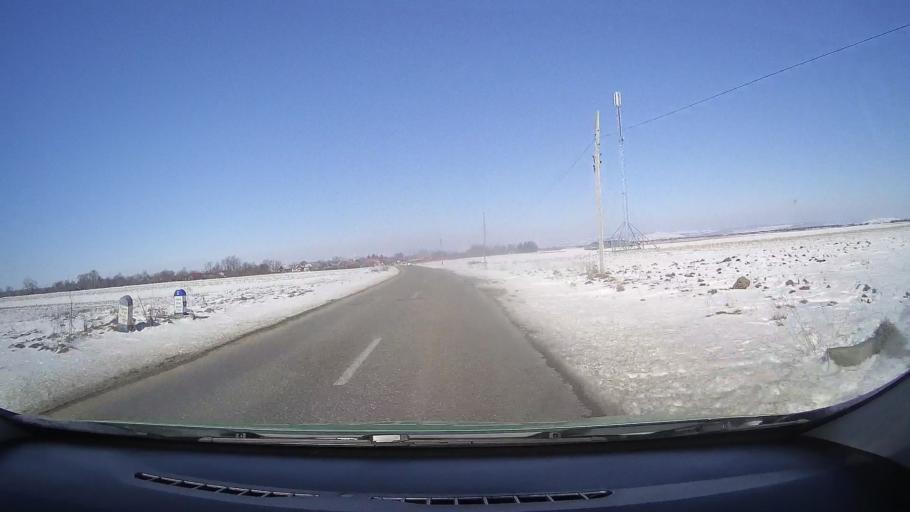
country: RO
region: Brasov
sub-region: Comuna Harseni
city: Harseni
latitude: 45.7471
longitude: 25.0168
